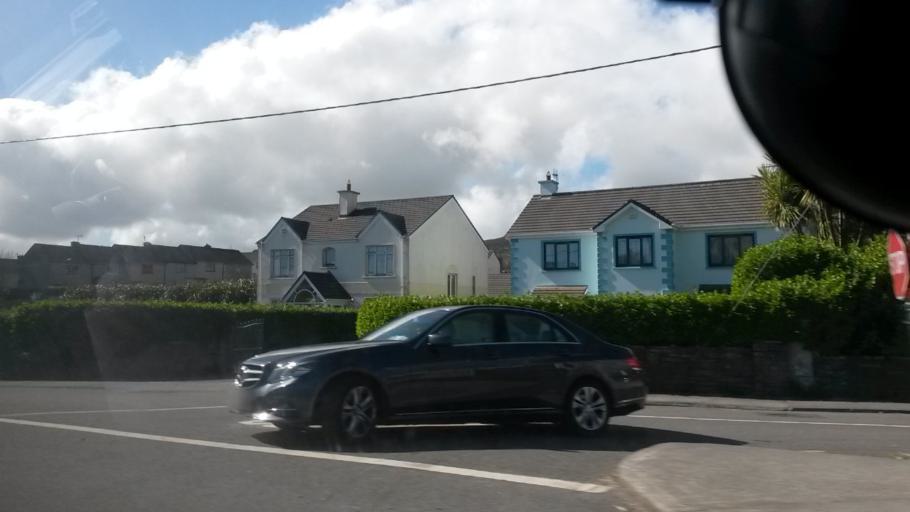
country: IE
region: Munster
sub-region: Ciarrai
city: Dingle
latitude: 52.1427
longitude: -10.2631
